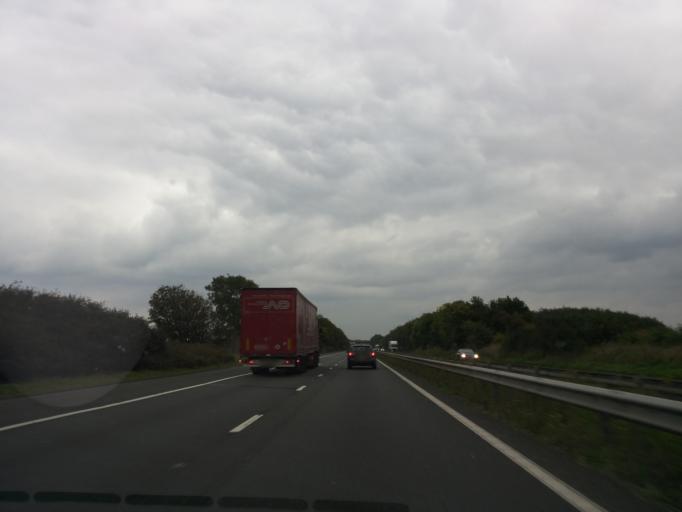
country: GB
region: England
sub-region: Kent
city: Sittingbourne
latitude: 51.2973
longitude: 0.7584
